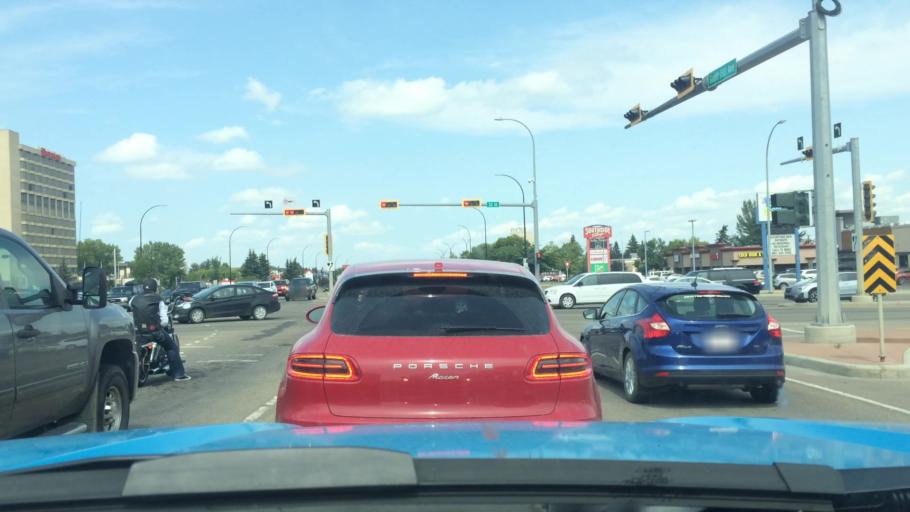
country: CA
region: Alberta
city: Red Deer
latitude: 52.2504
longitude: -113.8139
